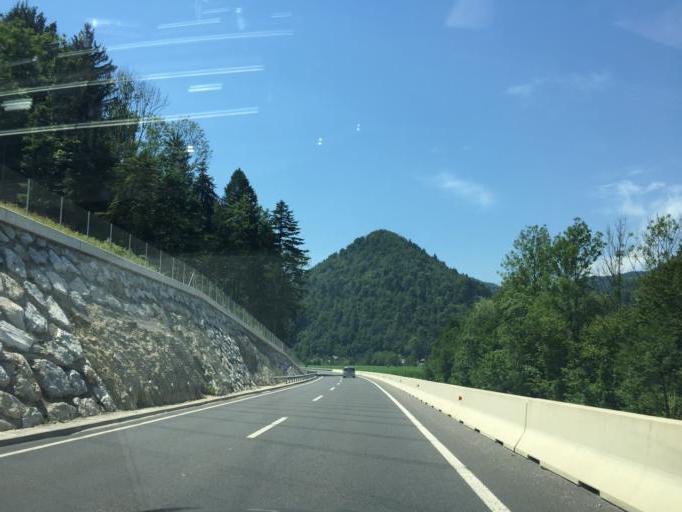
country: SI
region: Skofja Loka
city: Skofja Loka
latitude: 46.1542
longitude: 14.3001
